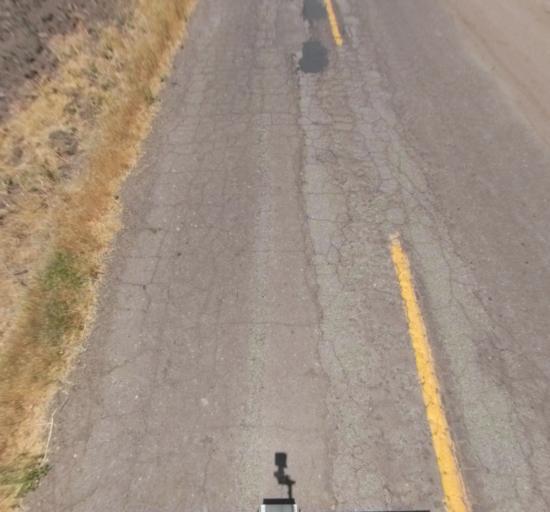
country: US
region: California
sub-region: Madera County
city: Chowchilla
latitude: 37.0280
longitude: -120.2925
